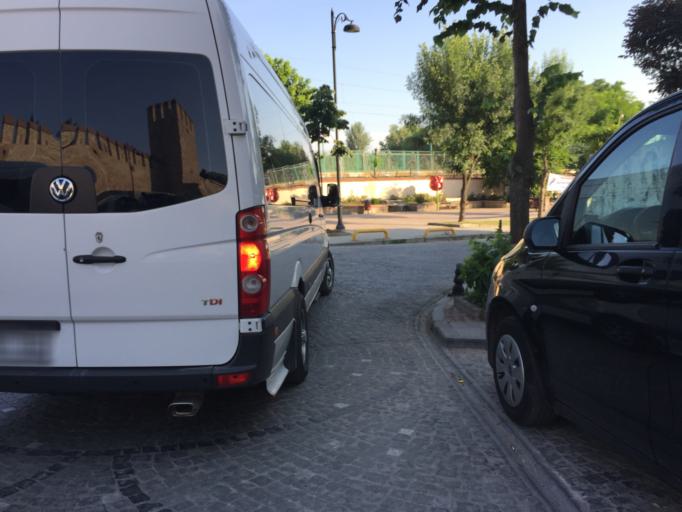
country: TR
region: Istanbul
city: Eminoenue
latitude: 41.0056
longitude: 28.9824
